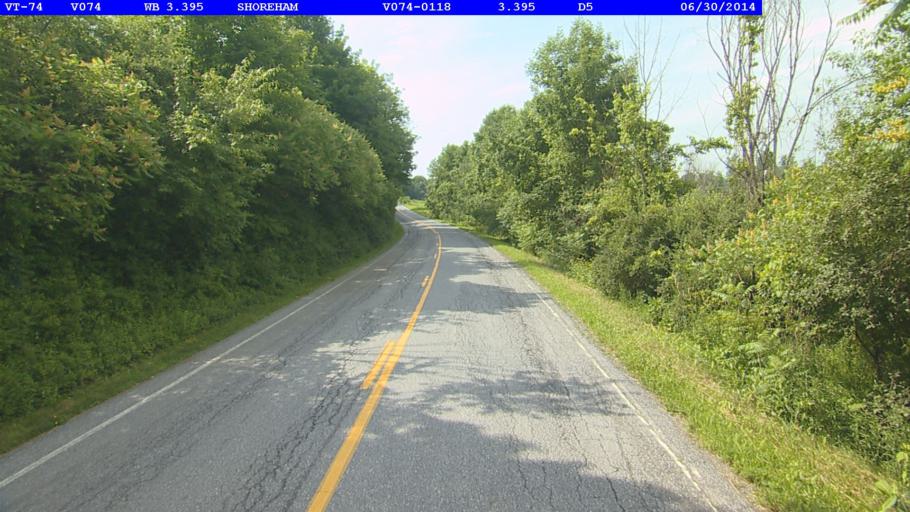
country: US
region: New York
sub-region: Essex County
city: Ticonderoga
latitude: 43.8807
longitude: -73.3336
